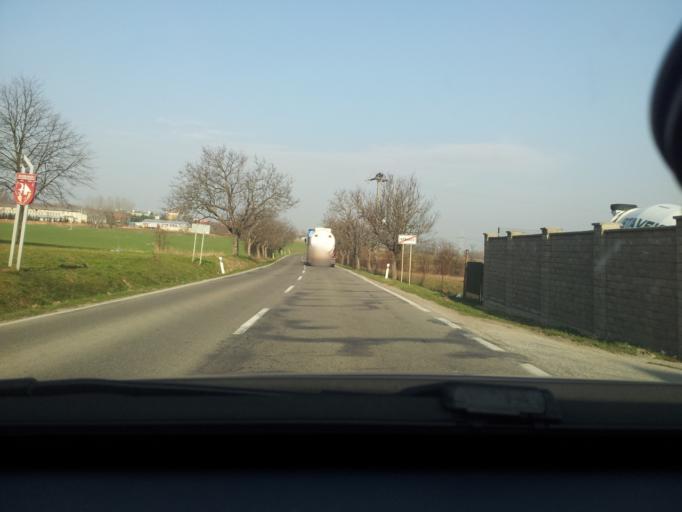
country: SK
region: Trnavsky
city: Hlohovec
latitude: 48.3723
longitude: 17.8880
